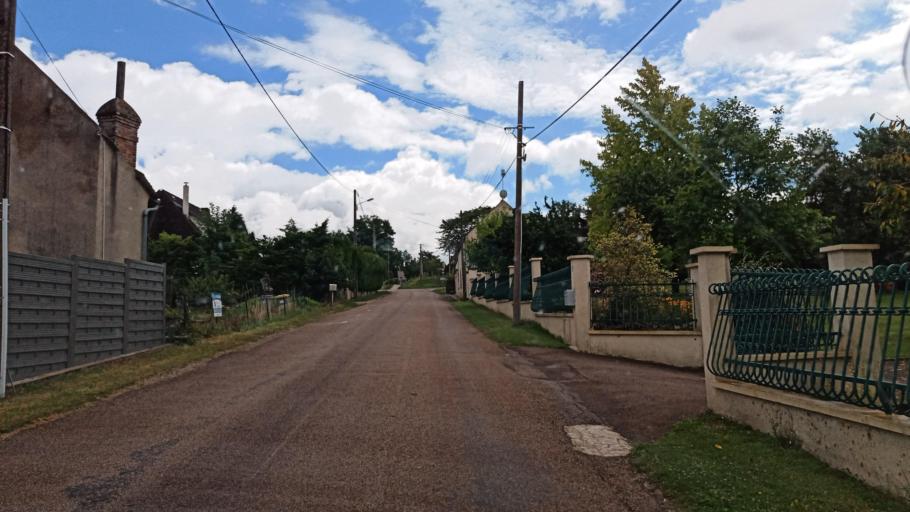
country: FR
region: Bourgogne
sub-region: Departement de l'Yonne
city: Cheroy
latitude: 48.2386
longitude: 3.0483
